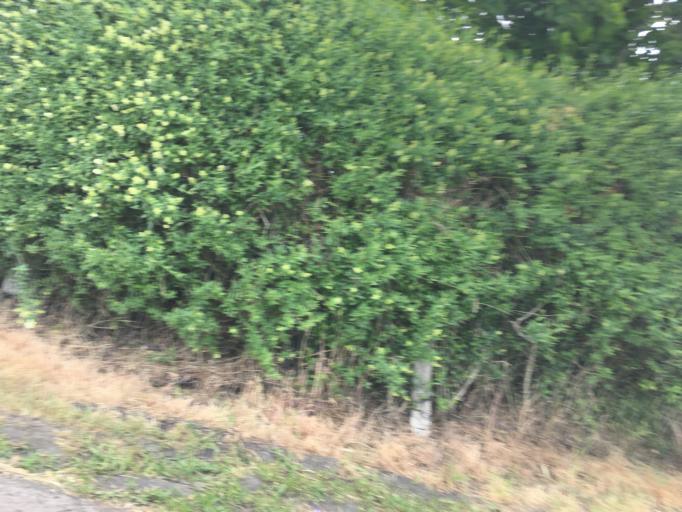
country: DE
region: Berlin
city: Falkenberg
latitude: 52.5799
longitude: 13.5370
